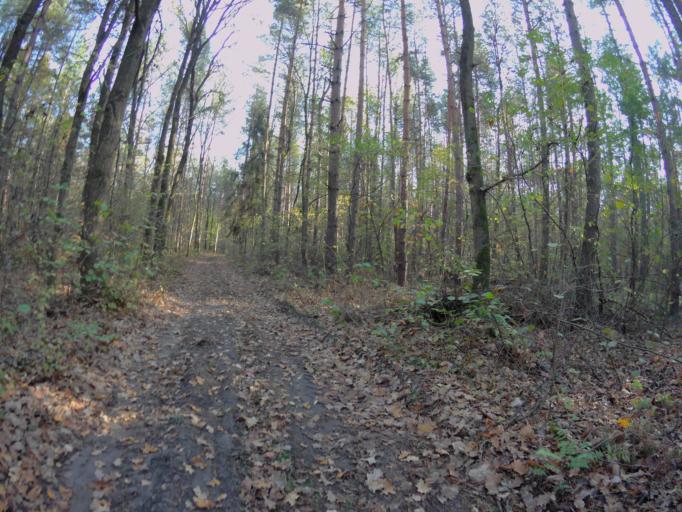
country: PL
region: Subcarpathian Voivodeship
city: Nowa Sarzyna
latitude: 50.3100
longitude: 22.3491
